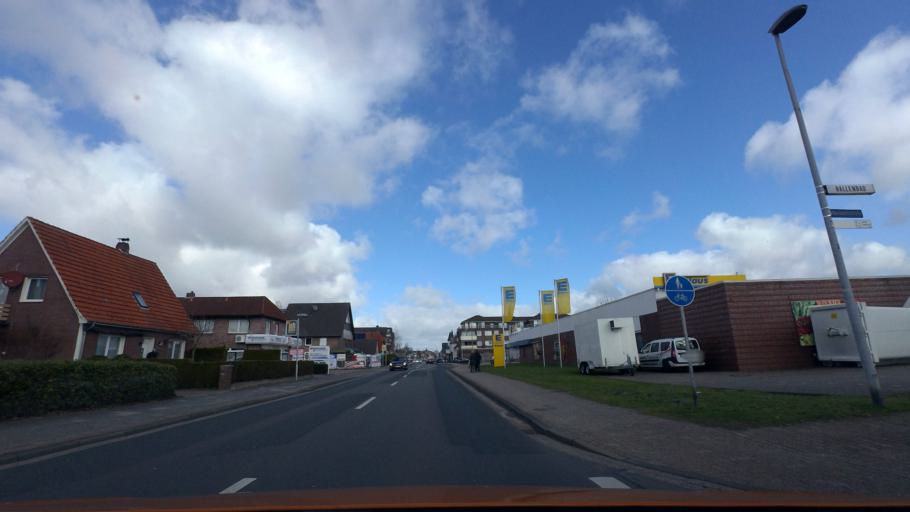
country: DE
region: Lower Saxony
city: Bad Zwischenahn
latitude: 53.1801
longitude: 7.9967
